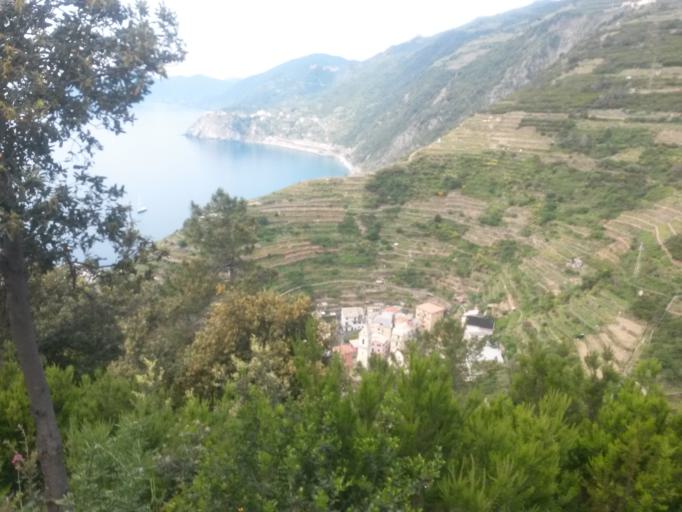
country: IT
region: Liguria
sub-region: Provincia di La Spezia
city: Riomaggiore
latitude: 44.1059
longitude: 9.7316
